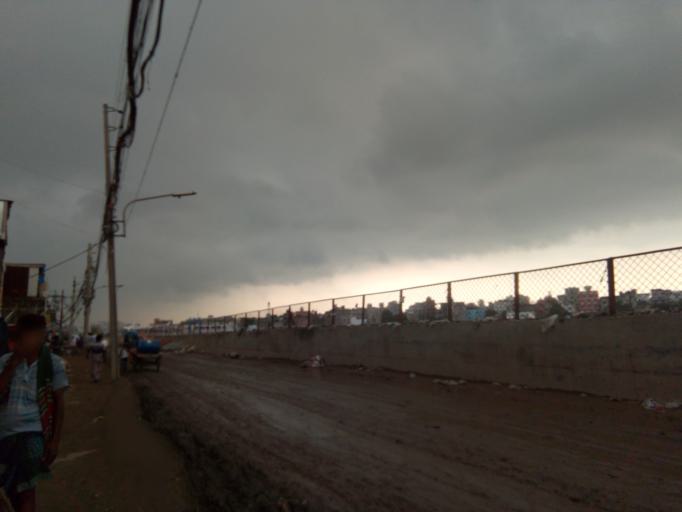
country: BD
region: Dhaka
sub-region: Dhaka
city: Dhaka
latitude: 23.7113
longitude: 90.3917
